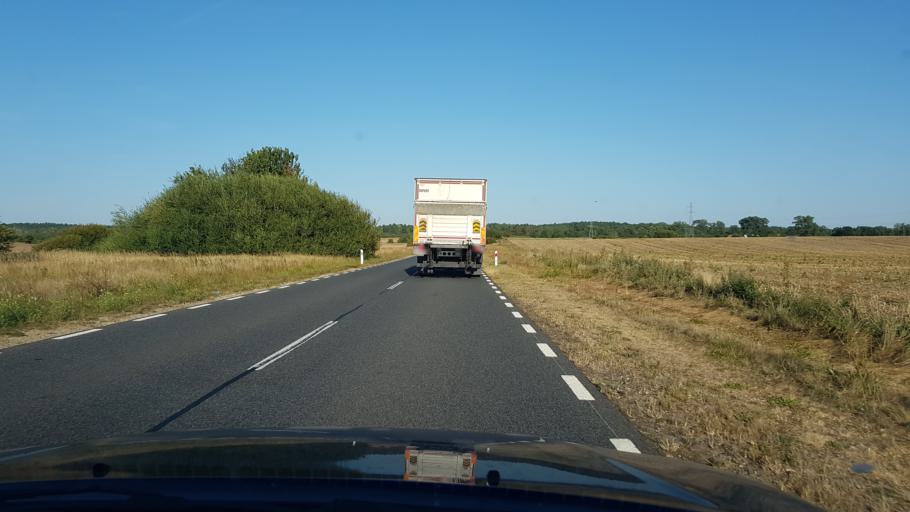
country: PL
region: West Pomeranian Voivodeship
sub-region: Powiat stargardzki
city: Stara Dabrowa
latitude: 53.4337
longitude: 15.1778
